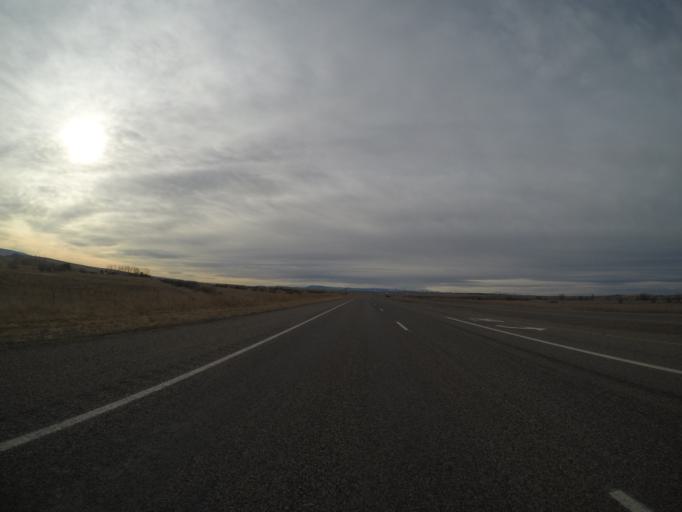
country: US
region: Montana
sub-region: Yellowstone County
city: Laurel
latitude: 45.5949
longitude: -108.8283
